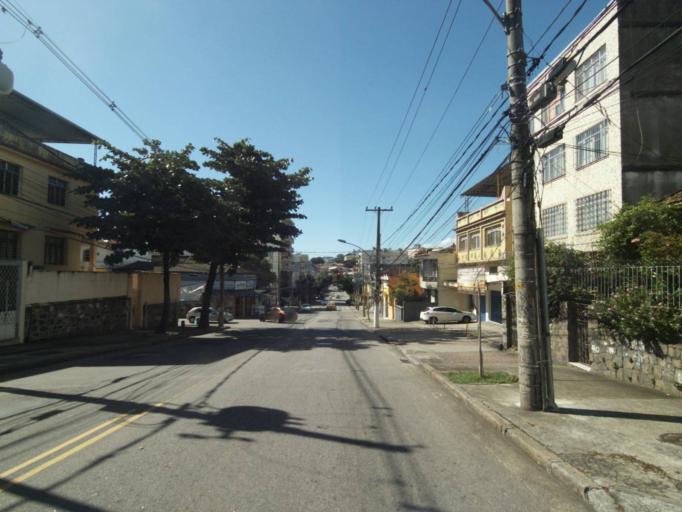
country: BR
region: Rio de Janeiro
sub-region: Rio De Janeiro
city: Rio de Janeiro
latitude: -22.9084
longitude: -43.2793
